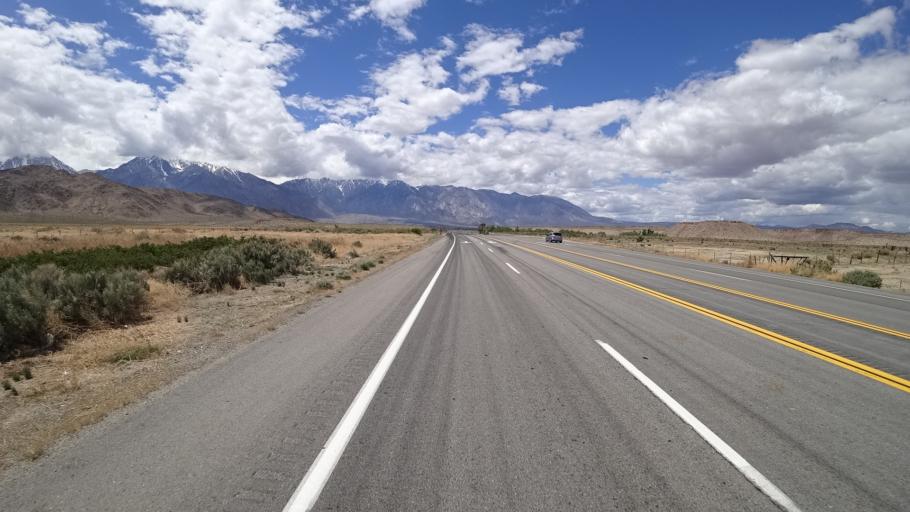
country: US
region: California
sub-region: Inyo County
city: West Bishop
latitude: 37.3868
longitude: -118.4934
